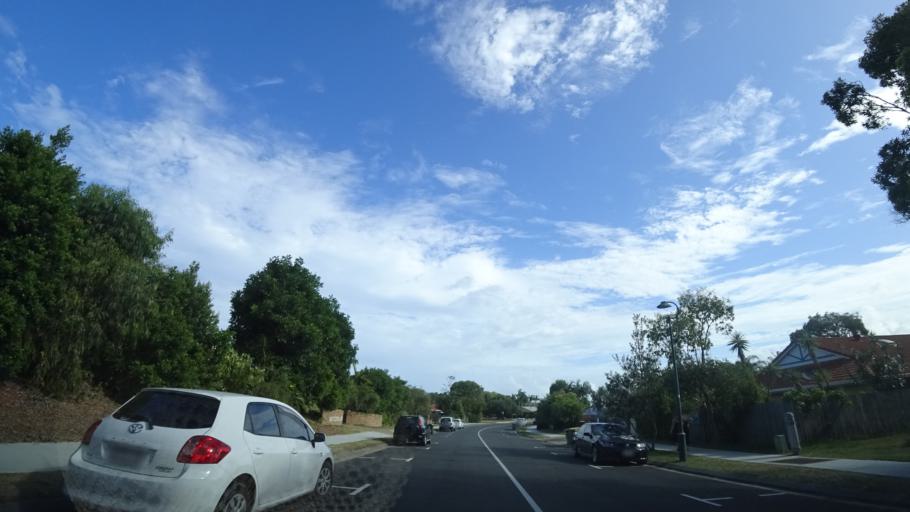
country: AU
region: Queensland
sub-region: Sunshine Coast
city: Coolum Beach
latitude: -26.5623
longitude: 153.0914
